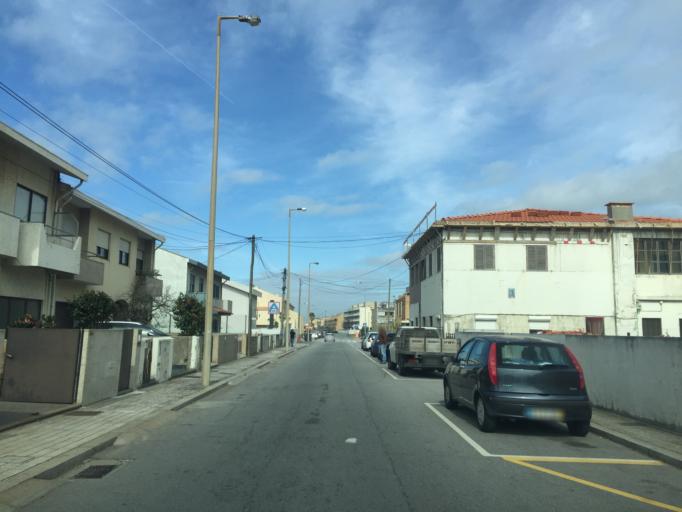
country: PT
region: Porto
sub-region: Matosinhos
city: Lavra
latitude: 41.2420
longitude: -8.7226
